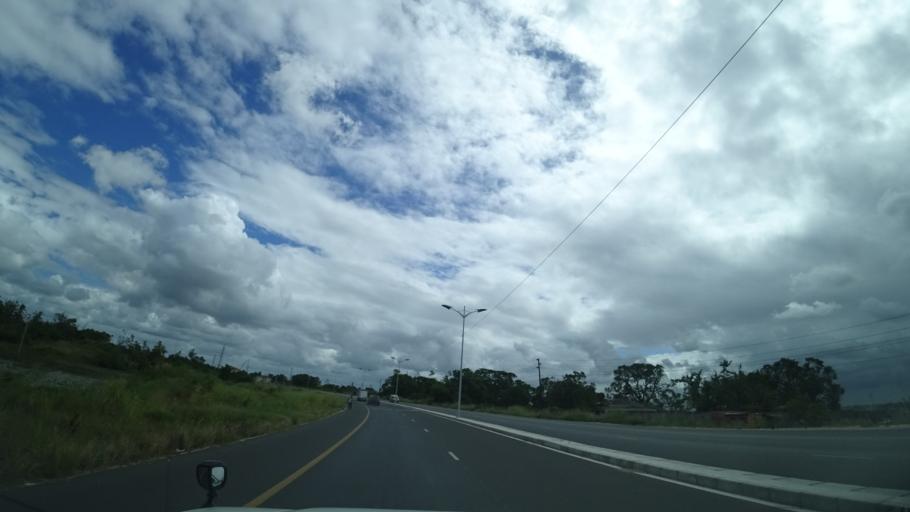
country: MZ
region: Sofala
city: Dondo
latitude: -19.5802
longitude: 34.7334
